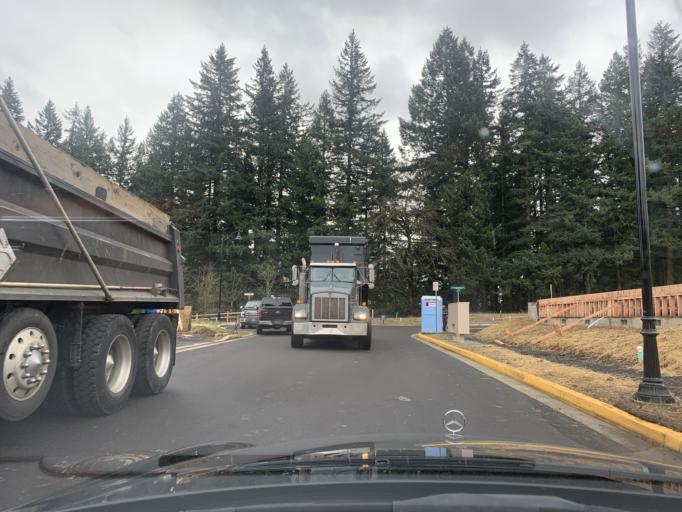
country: US
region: Oregon
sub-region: Clackamas County
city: Happy Valley
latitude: 45.4402
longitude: -122.5086
